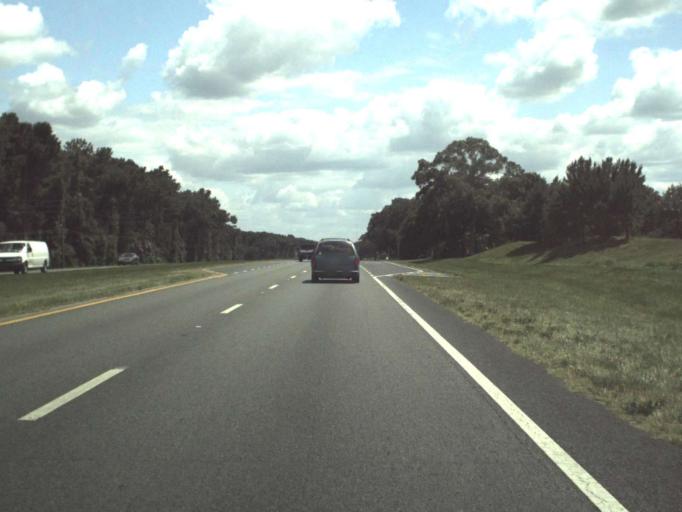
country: US
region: Florida
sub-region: Marion County
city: Ocala
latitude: 29.2779
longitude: -82.1521
